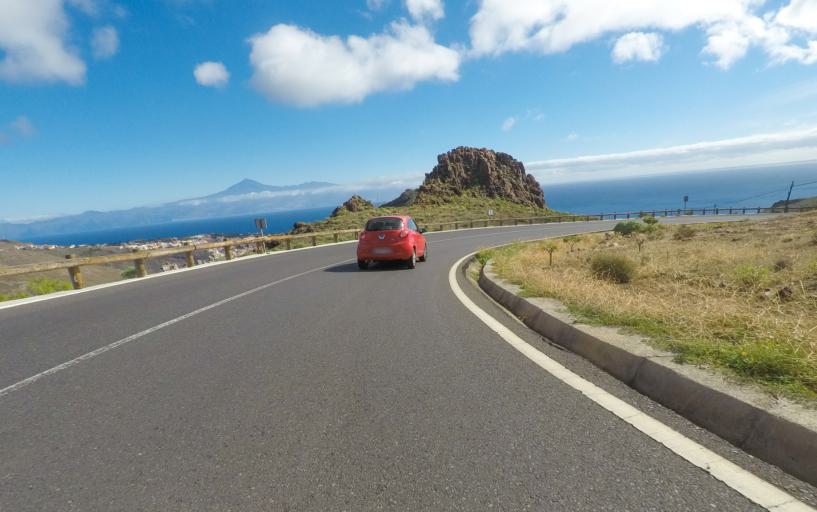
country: ES
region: Canary Islands
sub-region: Provincia de Santa Cruz de Tenerife
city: San Sebastian de la Gomera
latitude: 28.0841
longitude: -17.1295
